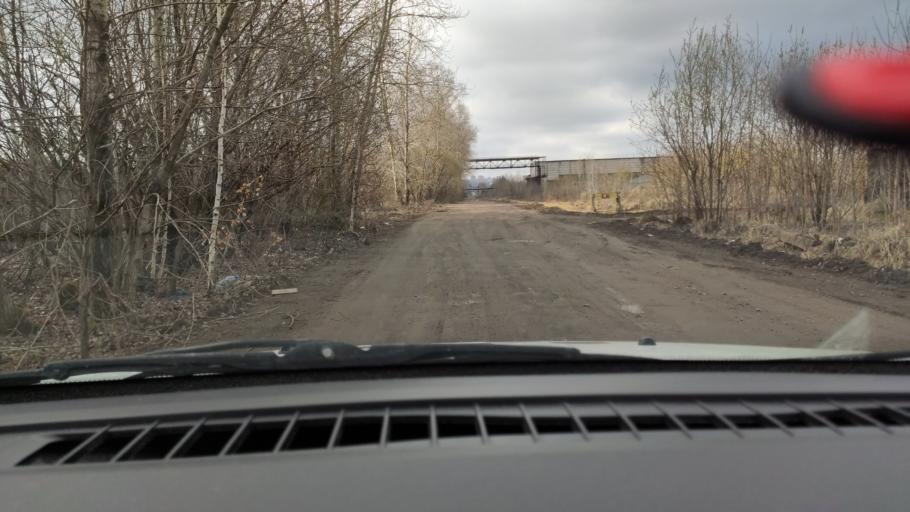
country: RU
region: Perm
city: Perm
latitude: 58.0533
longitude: 56.3224
